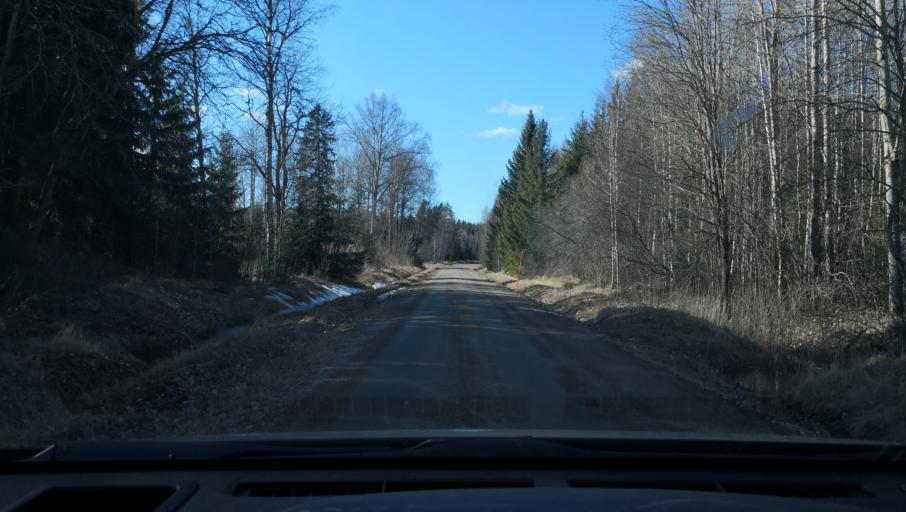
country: SE
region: Vaestmanland
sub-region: Sala Kommun
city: Sala
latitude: 60.1155
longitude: 16.6752
